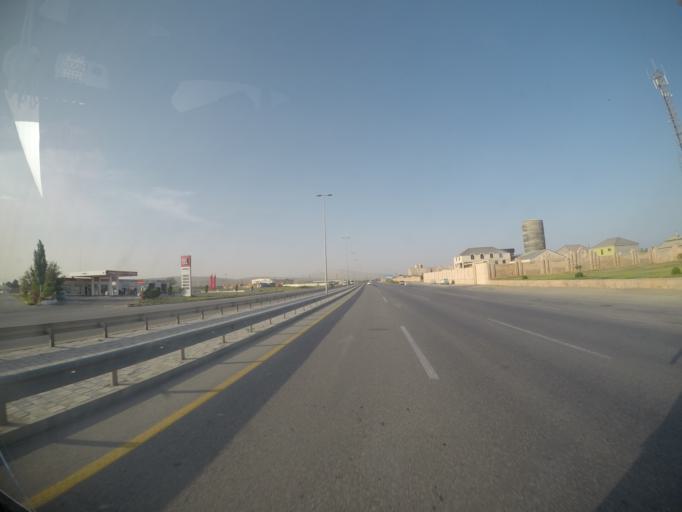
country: AZ
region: Baki
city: Korgoz
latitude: 40.2221
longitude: 49.5646
